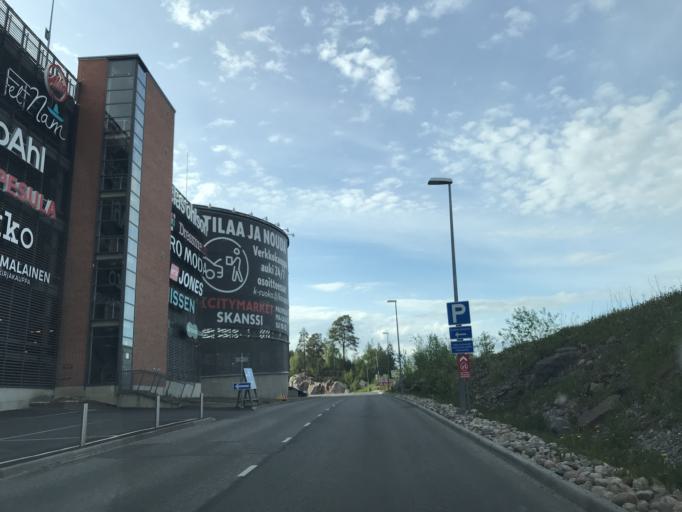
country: FI
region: Varsinais-Suomi
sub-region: Turku
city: Kaarina
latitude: 60.4295
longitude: 22.3240
